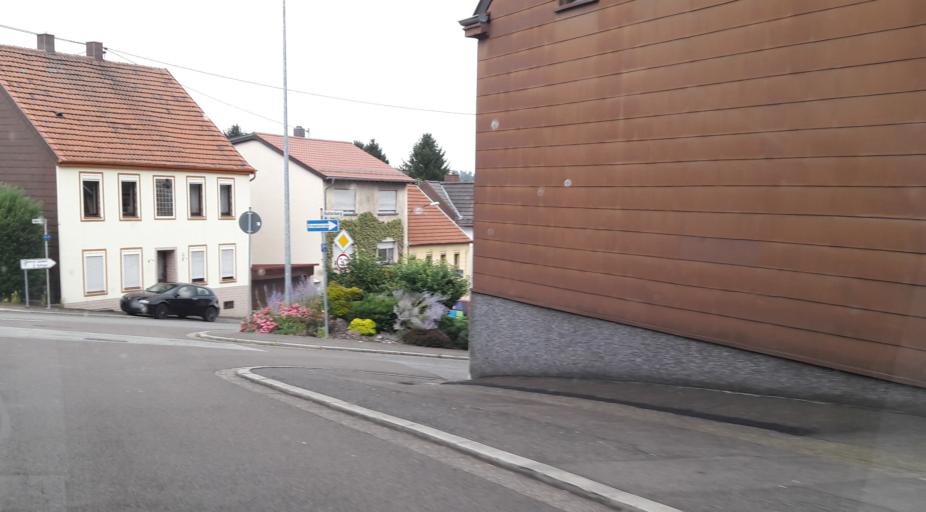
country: DE
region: Saarland
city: Spiesen-Elversberg
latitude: 49.3168
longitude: 7.1472
